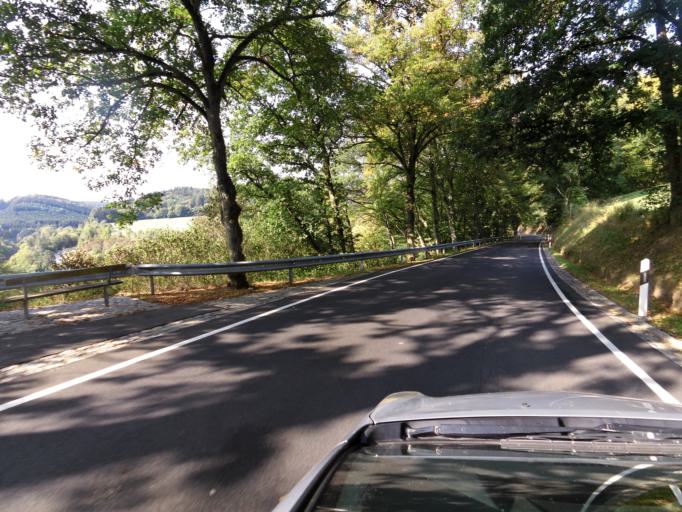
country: LU
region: Diekirch
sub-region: Canton de Wiltz
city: Goesdorf
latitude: 49.9077
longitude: 5.9619
